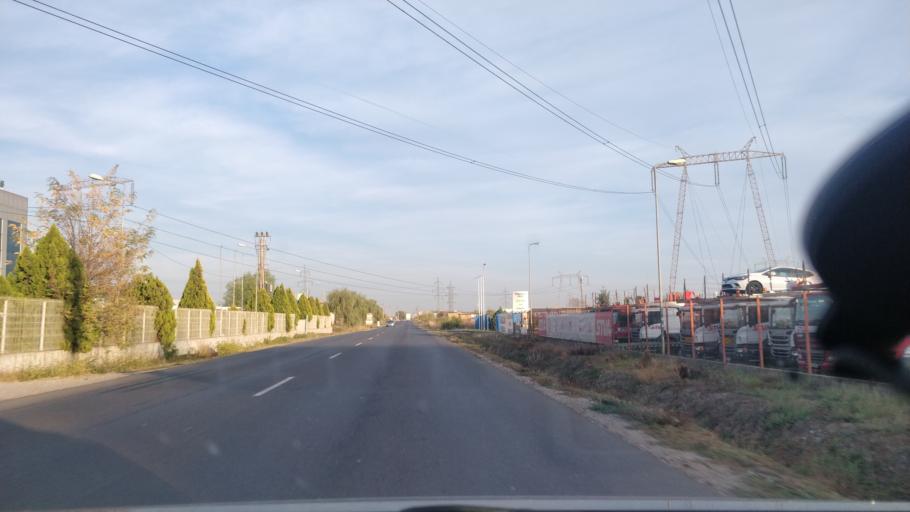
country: RO
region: Ilfov
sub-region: Comuna Ciorogarla
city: Ciorogarla
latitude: 44.4405
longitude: 25.9174
